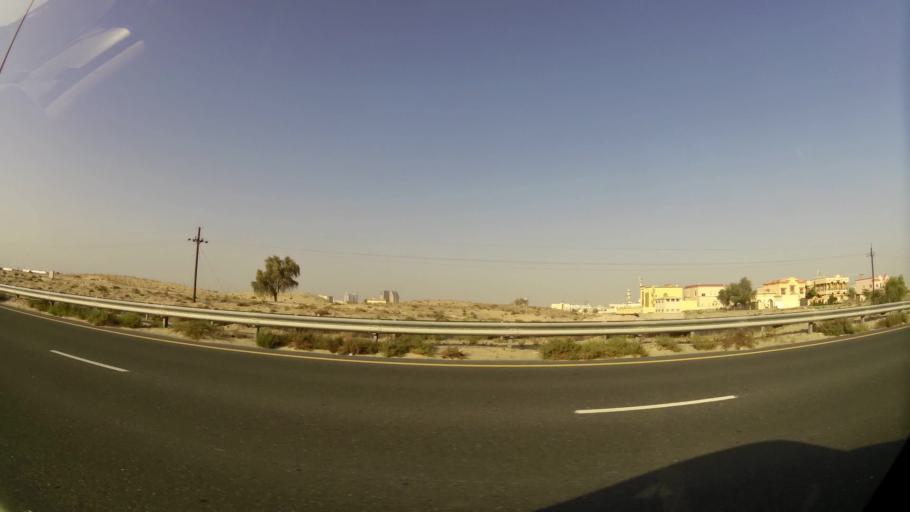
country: AE
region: Dubai
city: Dubai
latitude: 25.0651
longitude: 55.2201
